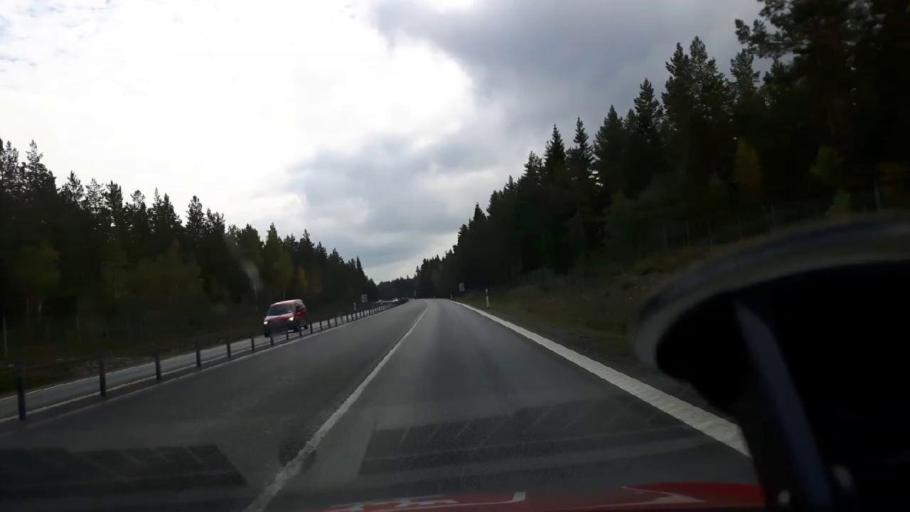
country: SE
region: Gaevleborg
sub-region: Gavle Kommun
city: Norrsundet
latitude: 60.8747
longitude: 17.0489
